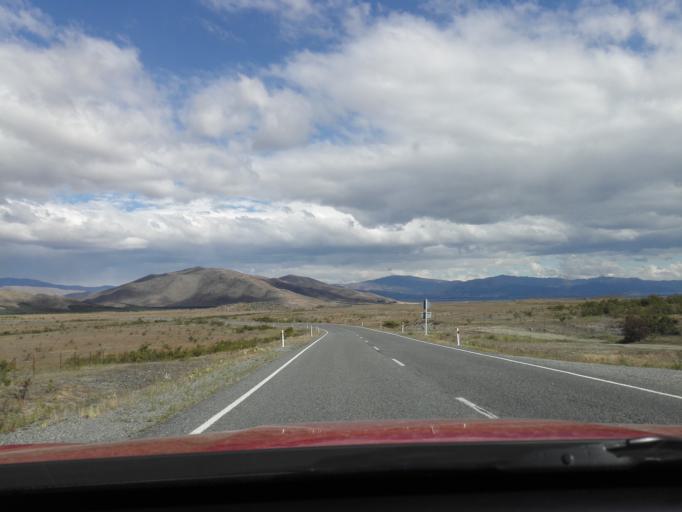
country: NZ
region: Canterbury
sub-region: Timaru District
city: Pleasant Point
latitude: -44.1982
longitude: 170.2482
